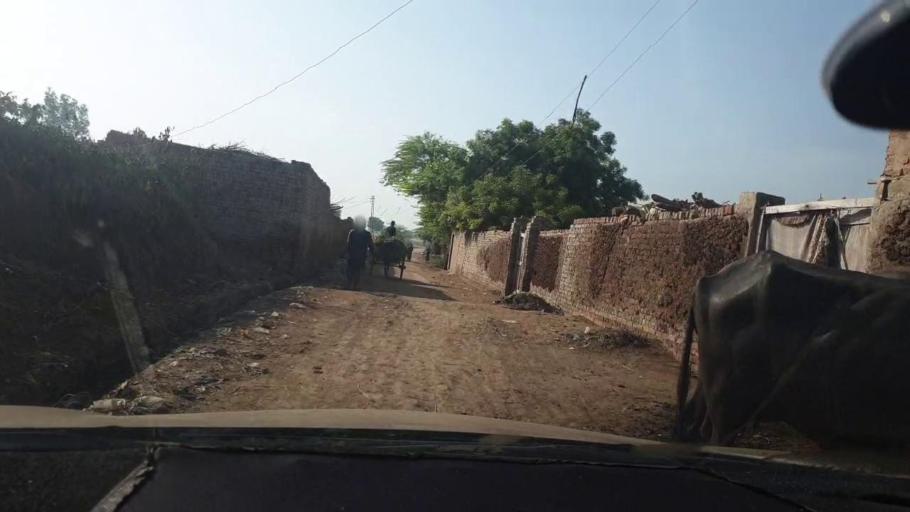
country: PK
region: Sindh
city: Kambar
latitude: 27.6459
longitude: 68.0414
